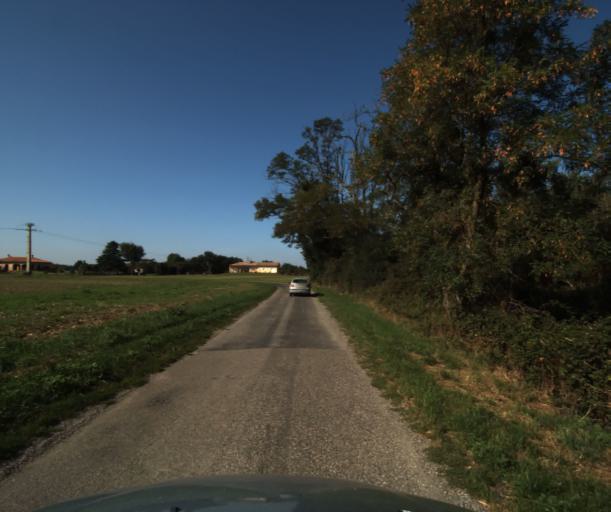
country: FR
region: Midi-Pyrenees
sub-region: Departement de la Haute-Garonne
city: Le Fauga
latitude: 43.4170
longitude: 1.3058
